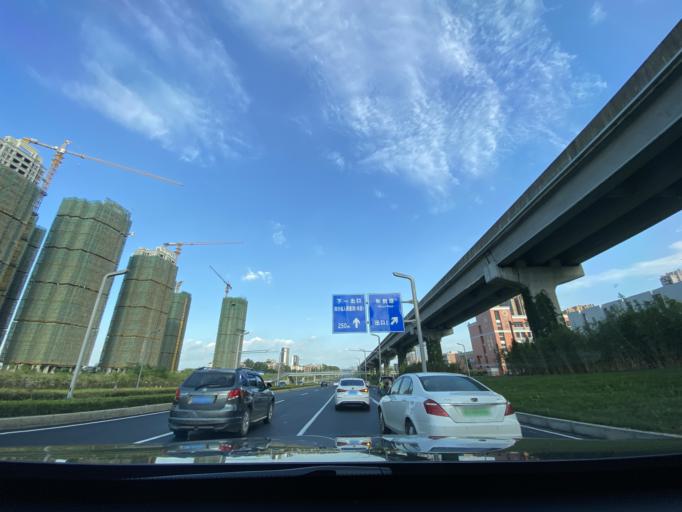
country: CN
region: Sichuan
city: Chengdu
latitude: 30.6342
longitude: 104.1555
